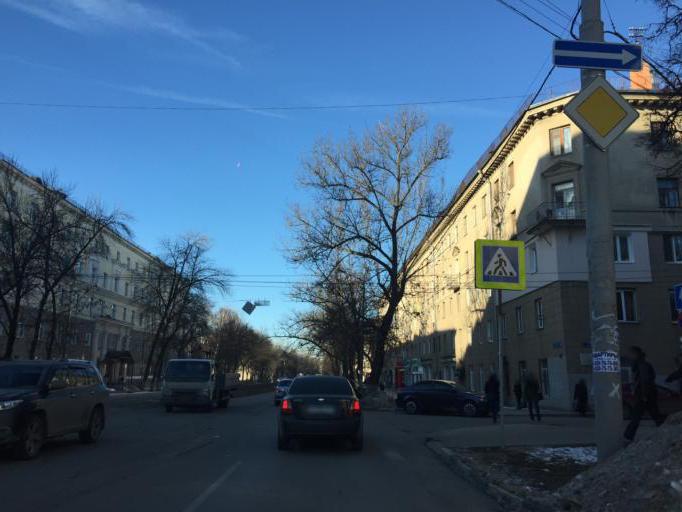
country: RU
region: Tula
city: Mendeleyevskiy
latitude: 54.1677
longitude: 37.5865
